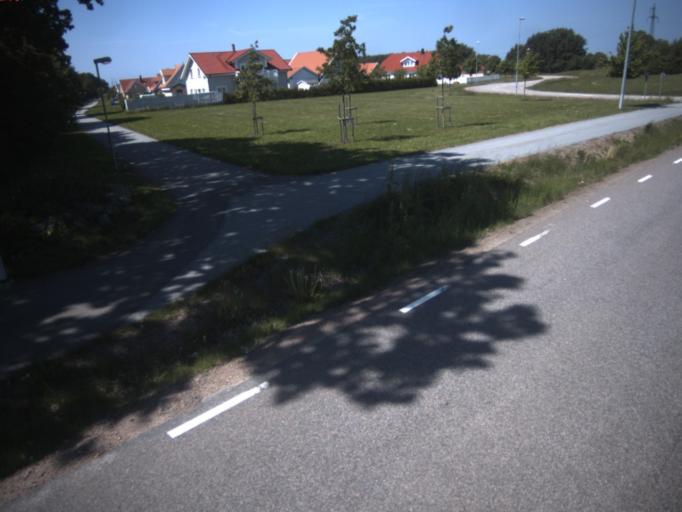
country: SE
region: Skane
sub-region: Helsingborg
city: Barslov
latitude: 56.0126
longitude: 12.8083
